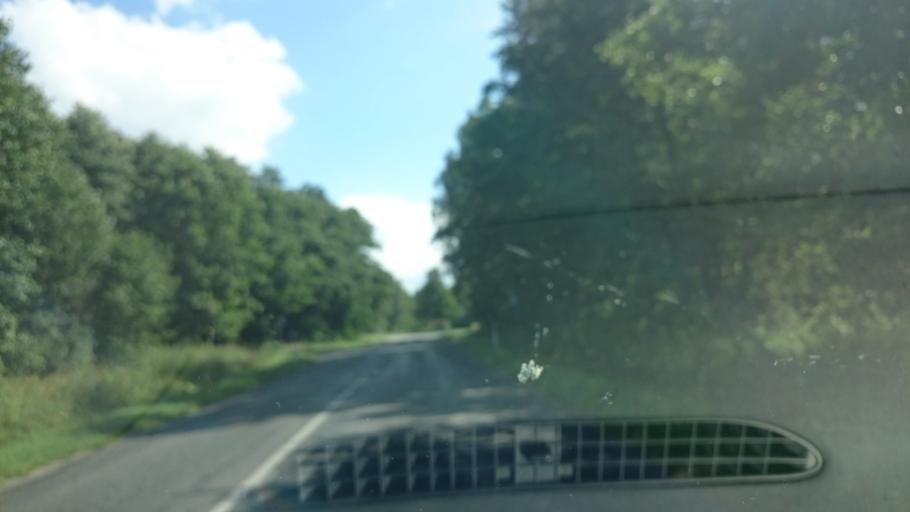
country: EE
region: Saare
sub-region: Orissaare vald
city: Orissaare
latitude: 58.5703
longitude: 22.7610
